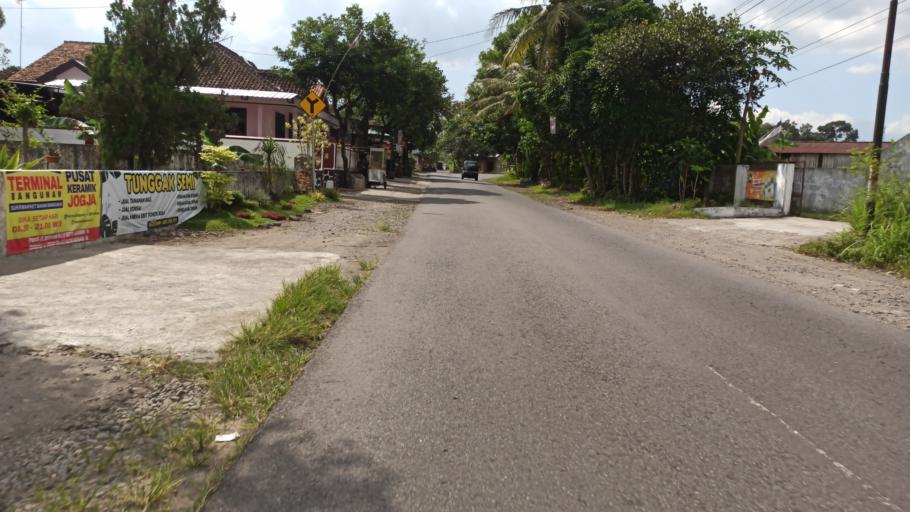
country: ID
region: Daerah Istimewa Yogyakarta
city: Sleman
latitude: -7.6823
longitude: 110.2989
